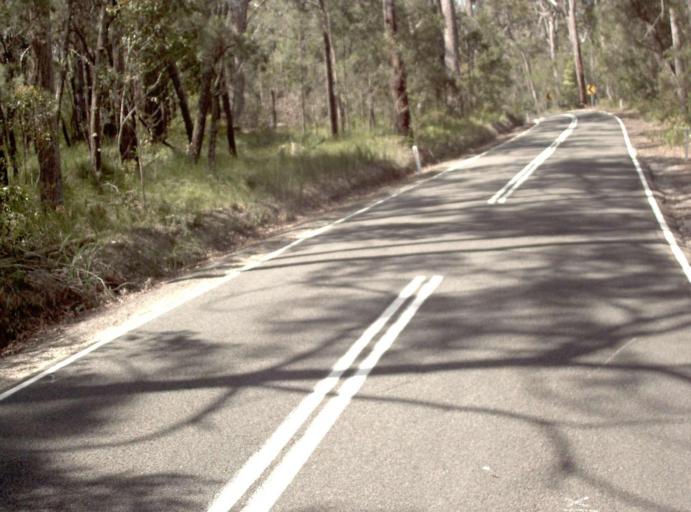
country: AU
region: New South Wales
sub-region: Bega Valley
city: Eden
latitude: -37.5182
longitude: 149.6873
